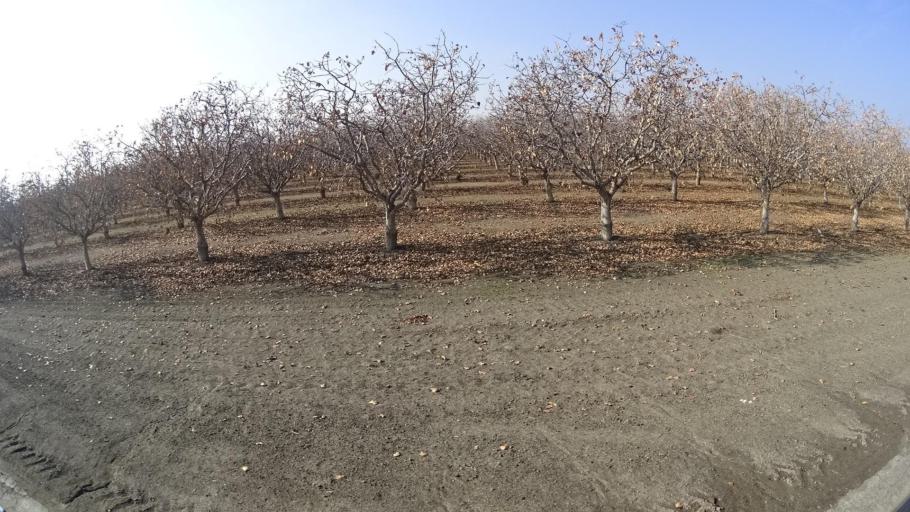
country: US
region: California
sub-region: Kern County
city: Buttonwillow
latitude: 35.3528
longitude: -119.4293
